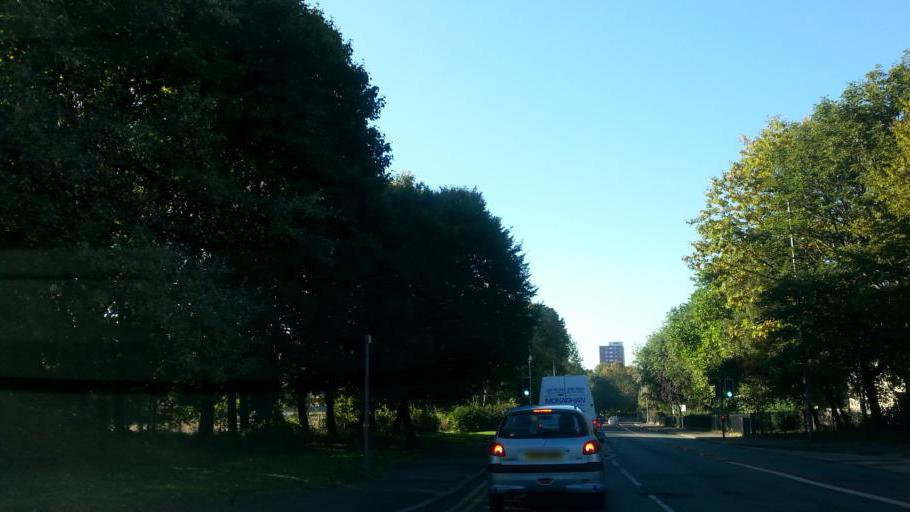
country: GB
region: England
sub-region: Manchester
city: Cheetham Hill
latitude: 53.4994
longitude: -2.2198
